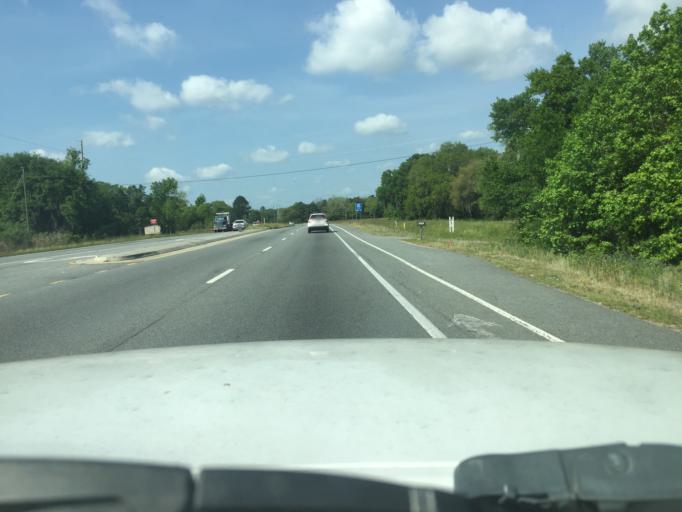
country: US
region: Georgia
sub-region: Chatham County
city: Georgetown
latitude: 32.0067
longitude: -81.2401
